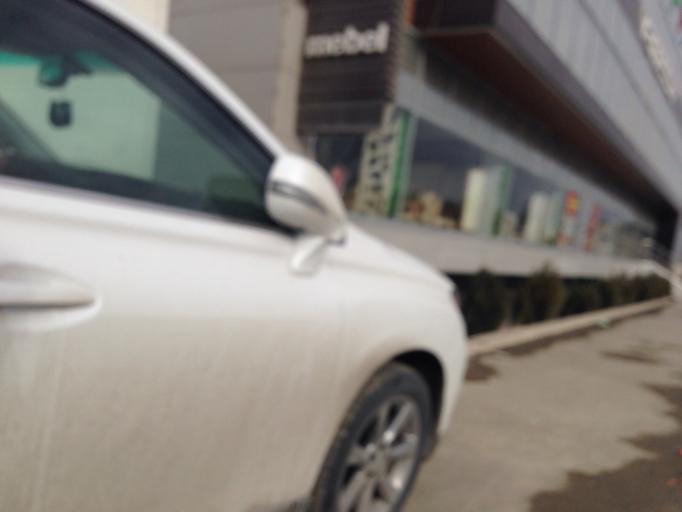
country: AZ
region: Baki
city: Baku
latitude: 40.3892
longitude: 49.8816
